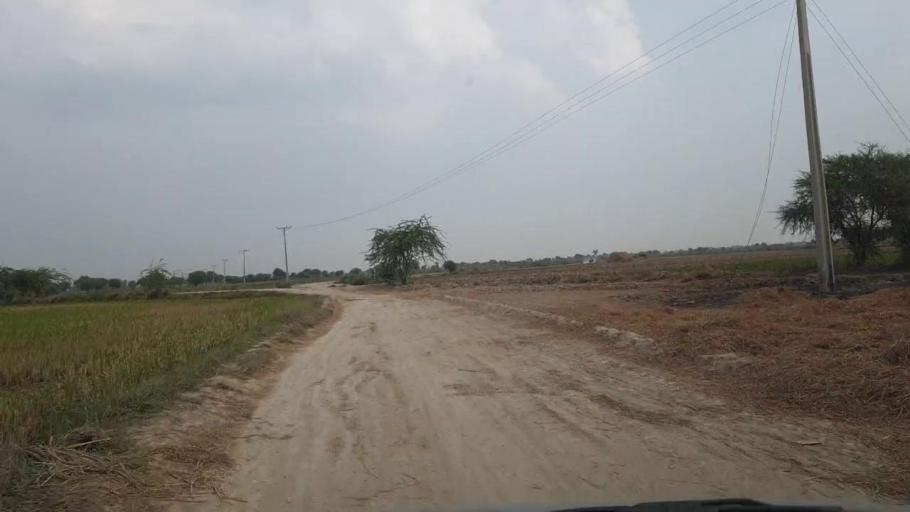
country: PK
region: Sindh
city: Matli
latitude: 24.9575
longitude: 68.7150
